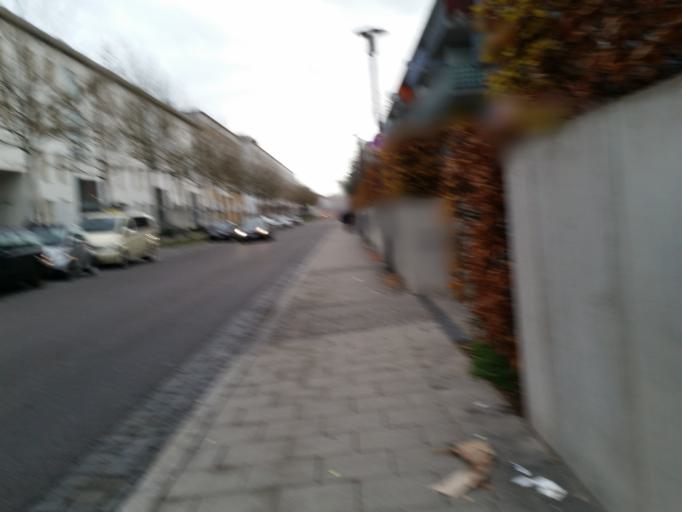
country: DE
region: Bavaria
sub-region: Upper Bavaria
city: Haar
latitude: 48.1301
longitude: 11.6890
